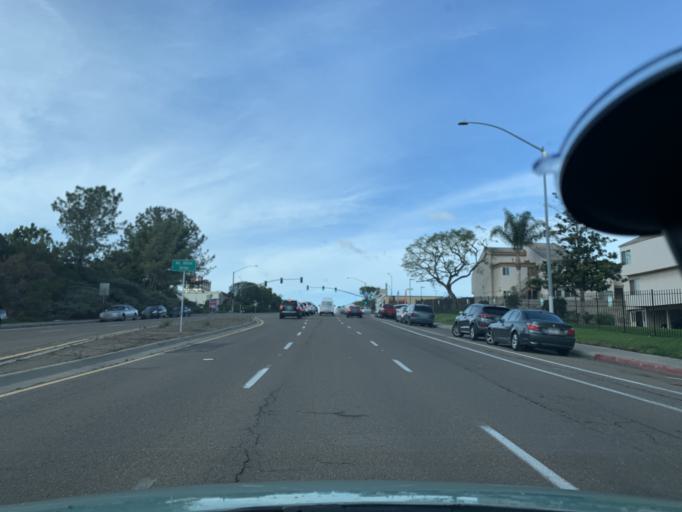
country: US
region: California
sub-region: San Diego County
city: La Jolla
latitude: 32.8162
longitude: -117.1802
